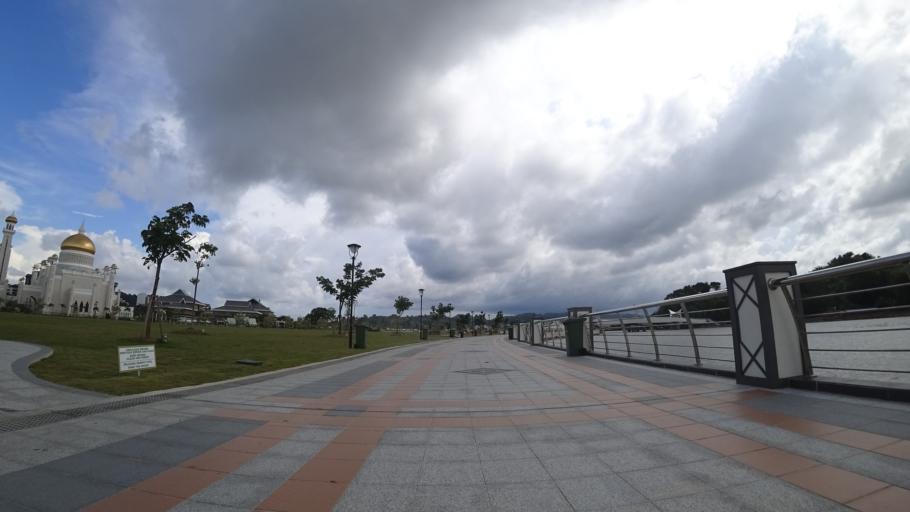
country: BN
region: Brunei and Muara
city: Bandar Seri Begawan
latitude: 4.8900
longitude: 114.9369
